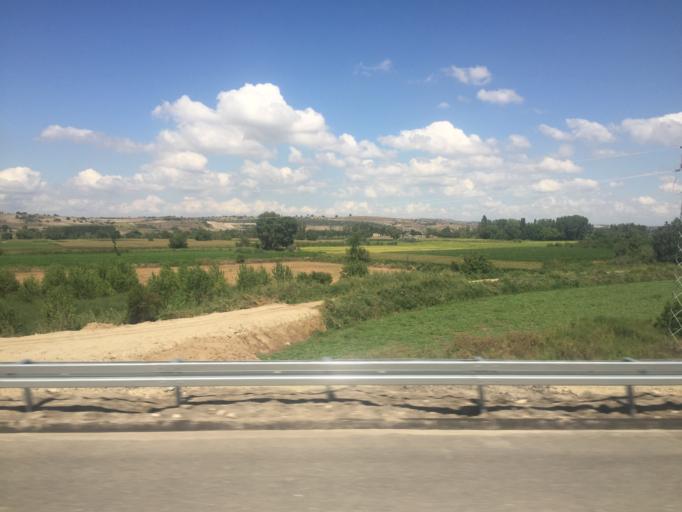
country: TR
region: Balikesir
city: Gobel
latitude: 39.9870
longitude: 28.1849
